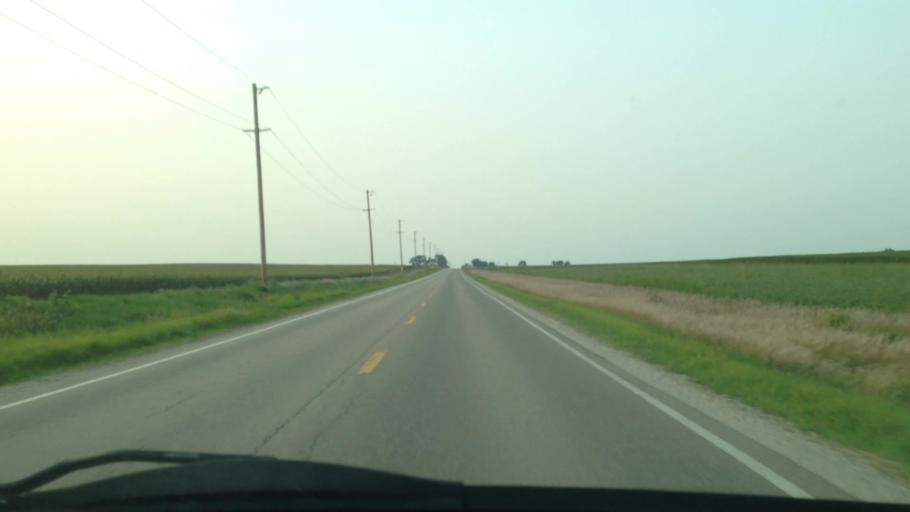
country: US
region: Iowa
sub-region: Iowa County
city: Marengo
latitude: 41.9526
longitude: -92.0852
